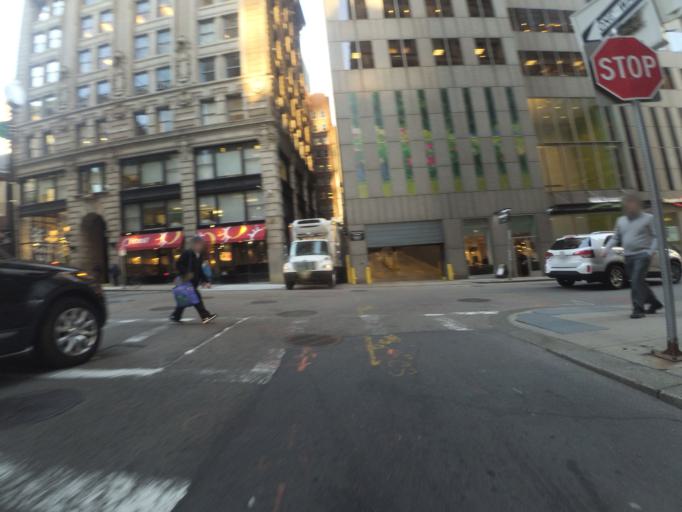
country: US
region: Massachusetts
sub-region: Suffolk County
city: Boston
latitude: 42.3567
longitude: -71.0577
